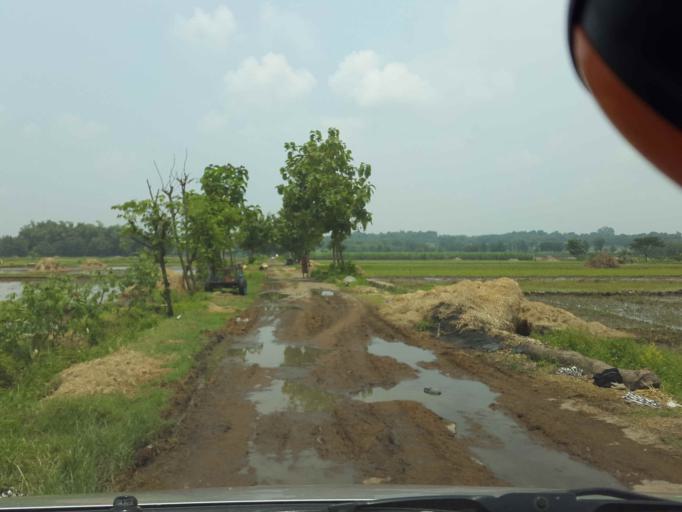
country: ID
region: Central Java
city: Surakarta
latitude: -7.4361
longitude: 110.8247
